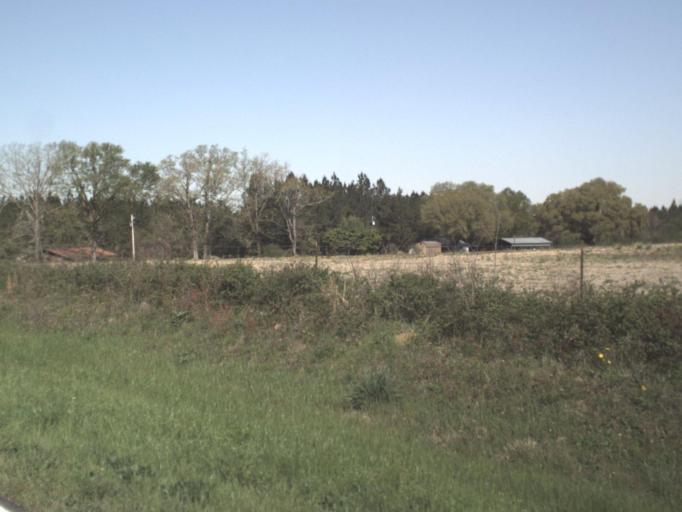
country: US
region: Florida
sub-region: Jackson County
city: Graceville
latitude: 30.9548
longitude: -85.4732
